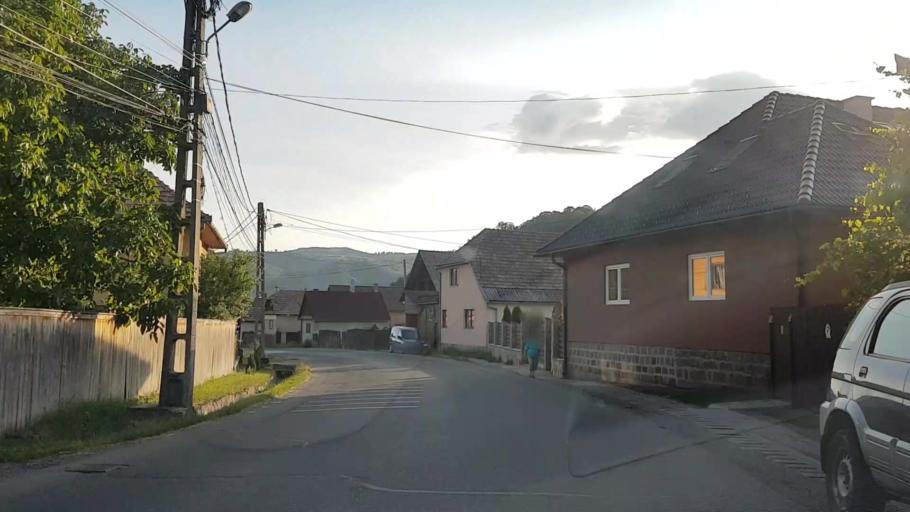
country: RO
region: Harghita
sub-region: Comuna Praid
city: Praid
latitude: 46.5576
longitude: 25.1314
